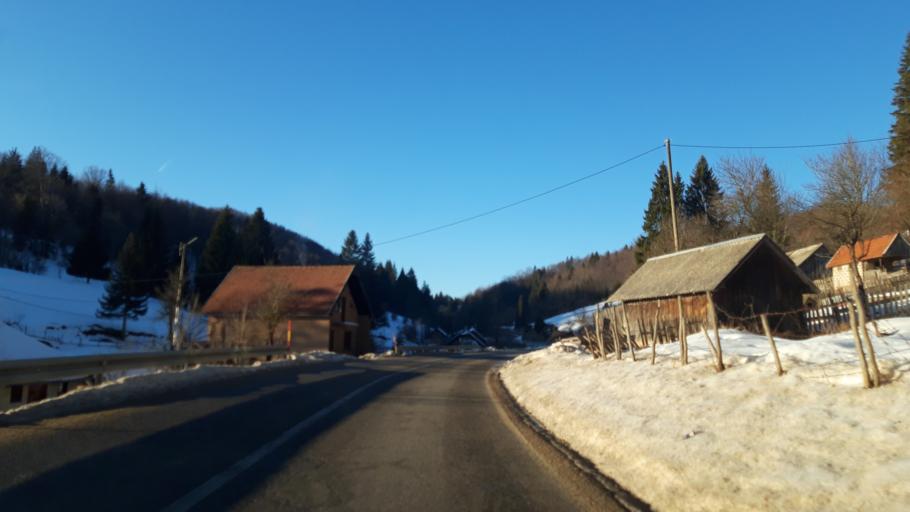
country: BA
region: Republika Srpska
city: Han Pijesak
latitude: 44.1251
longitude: 18.9635
